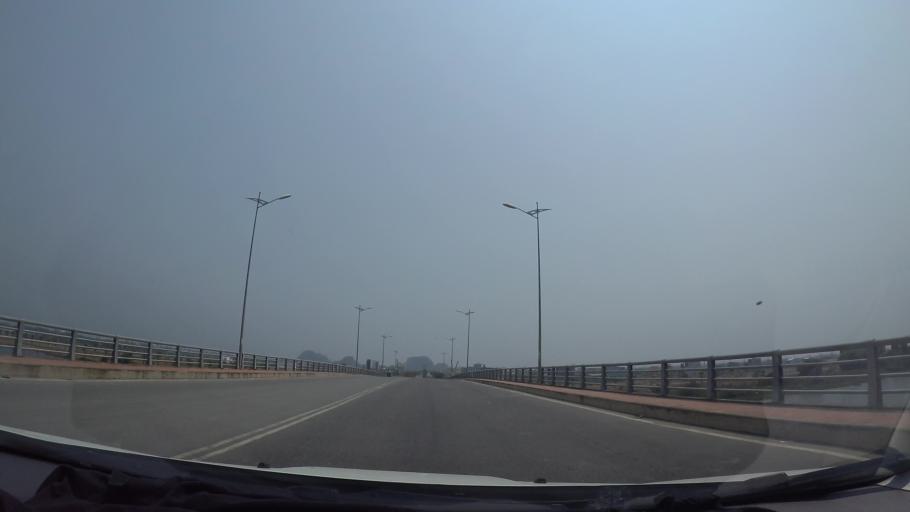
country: VN
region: Da Nang
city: Ngu Hanh Son
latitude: 16.0152
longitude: 108.2352
